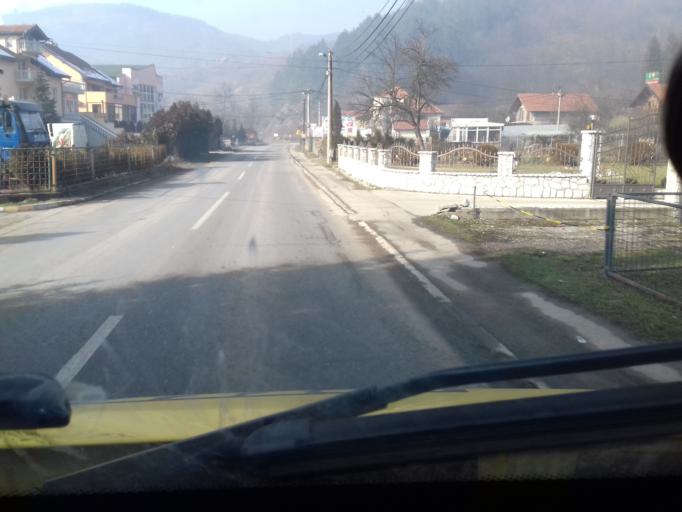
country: BA
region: Federation of Bosnia and Herzegovina
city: Mahala
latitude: 43.9969
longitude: 18.2178
